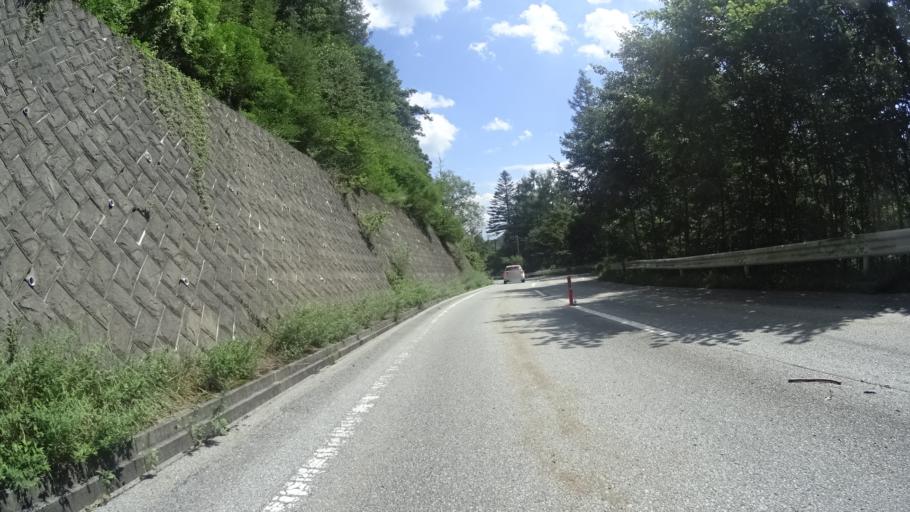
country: JP
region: Yamanashi
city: Enzan
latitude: 35.8040
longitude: 138.6667
